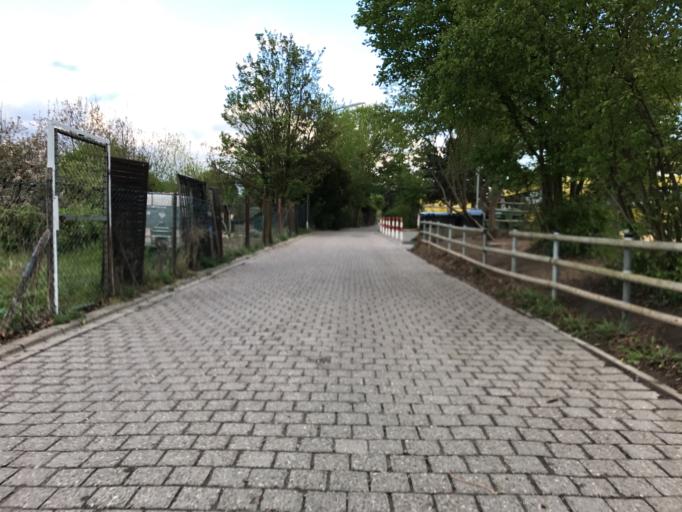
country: DE
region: Rheinland-Pfalz
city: Wackernheim
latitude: 49.9944
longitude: 8.1210
